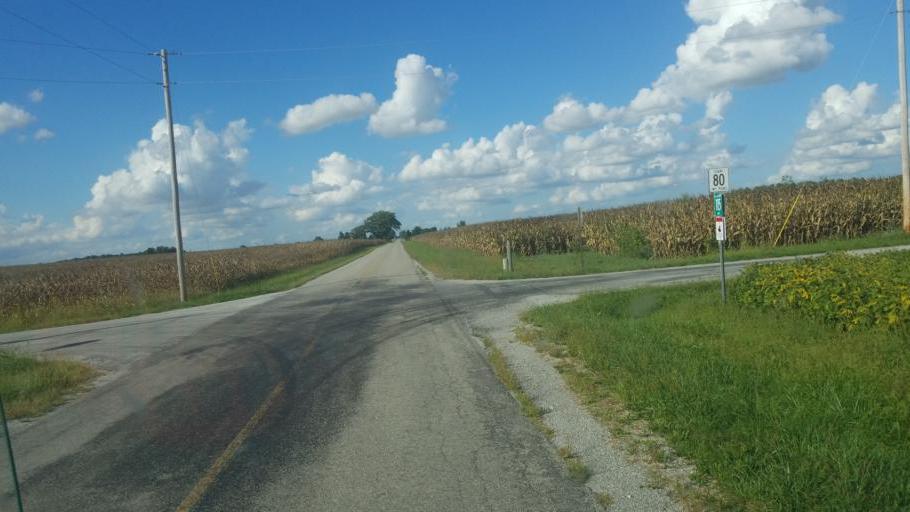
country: US
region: Ohio
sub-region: Hardin County
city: Kenton
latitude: 40.7179
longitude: -83.6917
